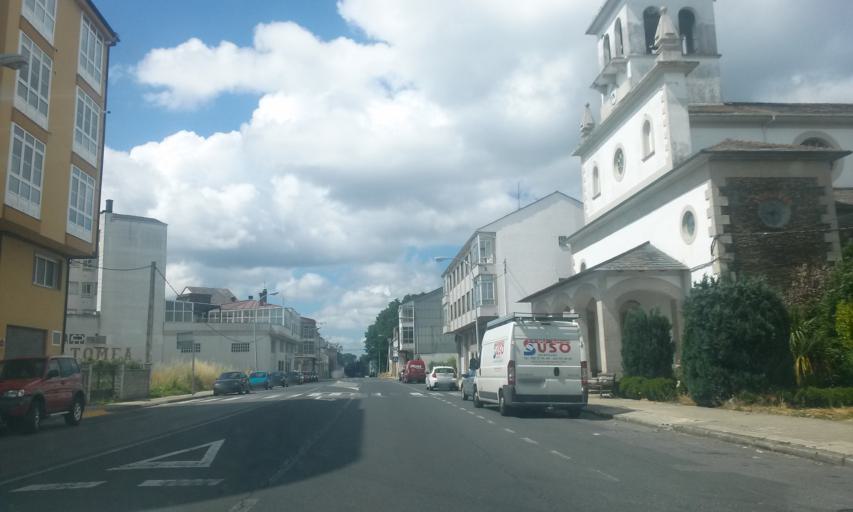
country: ES
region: Galicia
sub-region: Provincia de Lugo
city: Rabade
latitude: 43.1230
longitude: -7.6211
